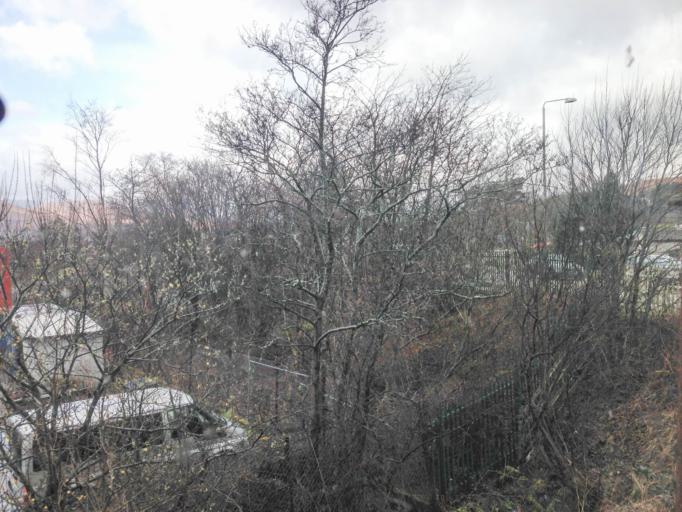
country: GB
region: Scotland
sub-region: Highland
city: Fort William
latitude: 56.8431
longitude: -5.0947
